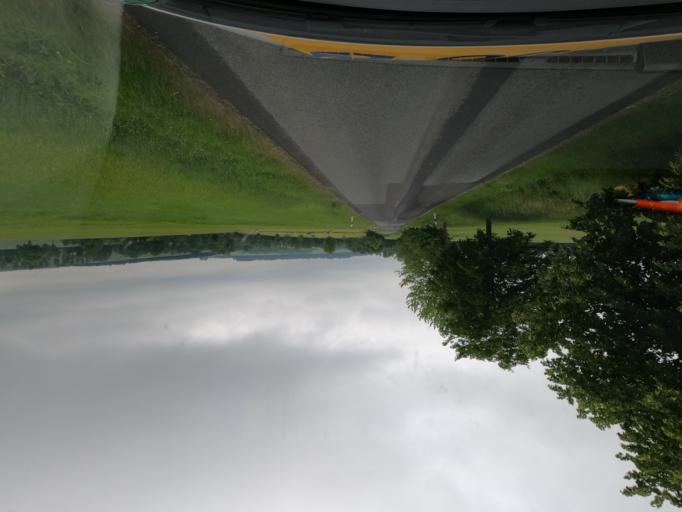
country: DE
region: Thuringia
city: Kreuzebra
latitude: 51.3358
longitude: 10.2640
